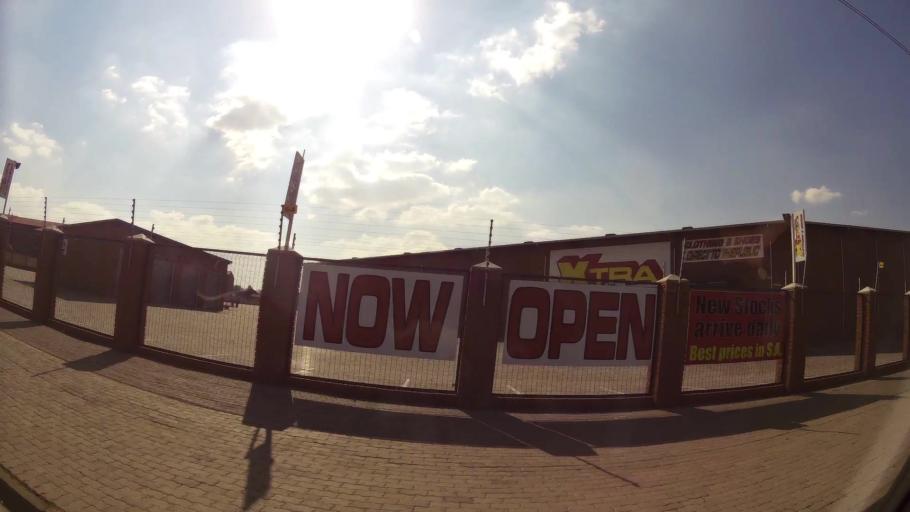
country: ZA
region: Gauteng
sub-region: Ekurhuleni Metropolitan Municipality
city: Boksburg
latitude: -26.2080
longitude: 28.2476
